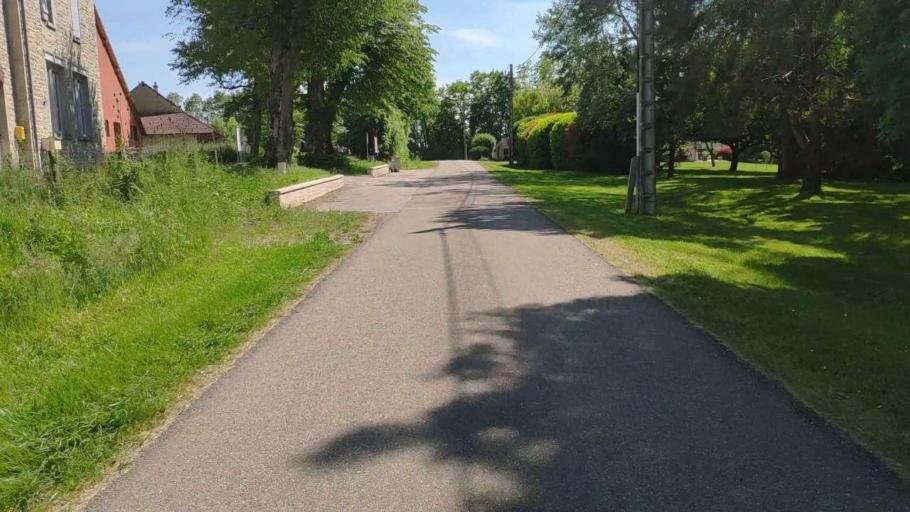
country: FR
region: Franche-Comte
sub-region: Departement du Jura
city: Bletterans
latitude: 46.8034
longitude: 5.4094
